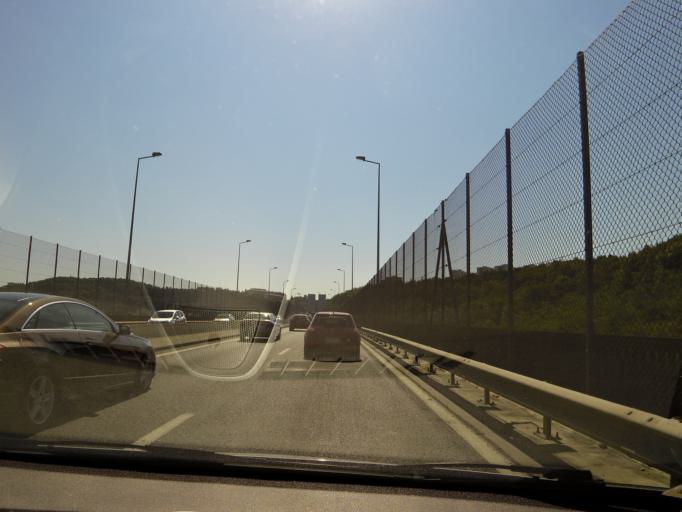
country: FR
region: Rhone-Alpes
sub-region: Departement du Rhone
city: Tassin-la-Demi-Lune
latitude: 45.7689
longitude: 4.7939
